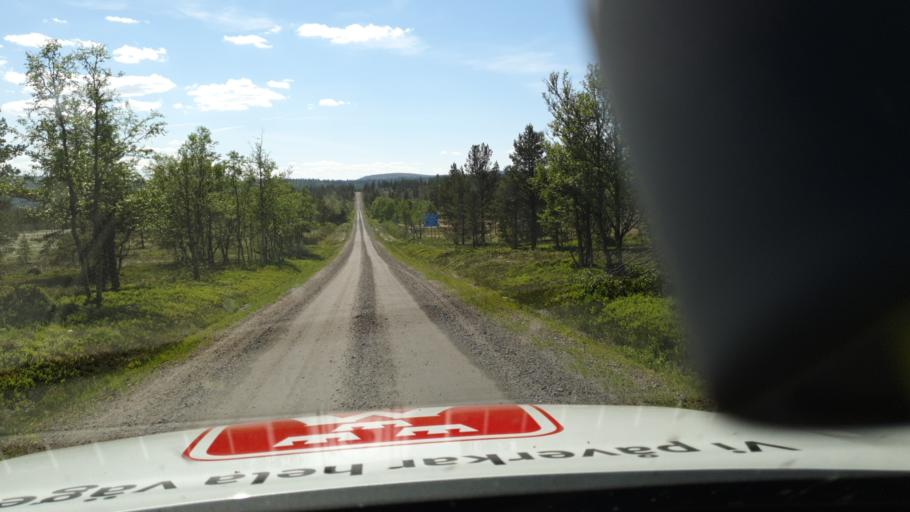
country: NO
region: Hedmark
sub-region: Engerdal
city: Engerdal
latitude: 62.1375
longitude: 12.9331
